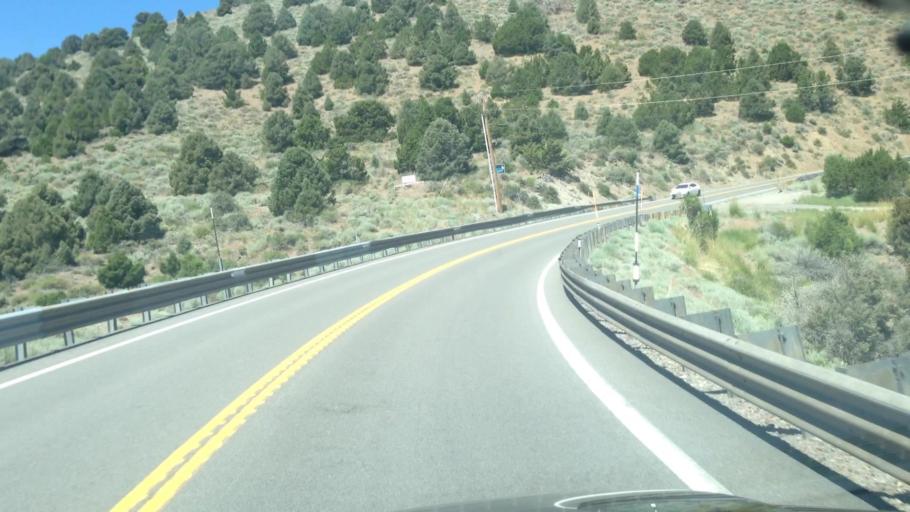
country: US
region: Nevada
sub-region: Storey County
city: Virginia City
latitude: 39.3490
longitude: -119.6432
